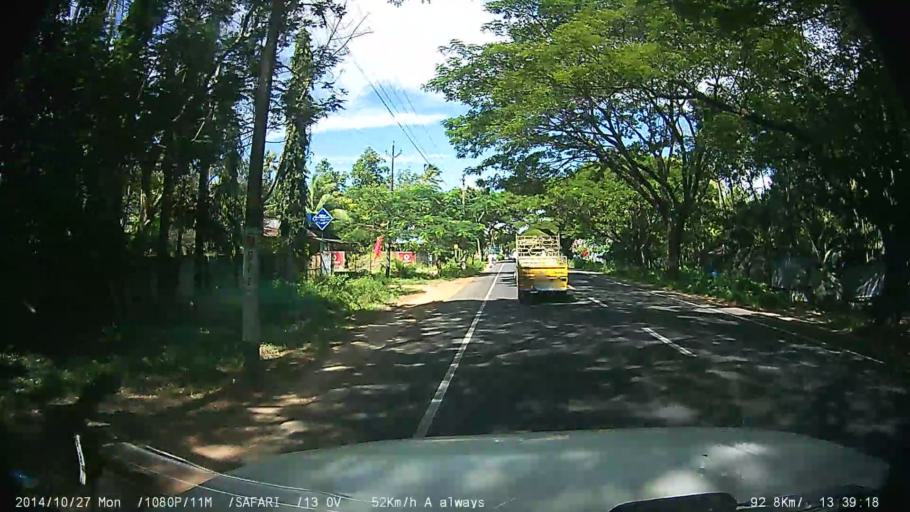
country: IN
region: Kerala
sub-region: Alappuzha
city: Shertallai
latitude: 9.6258
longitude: 76.3325
